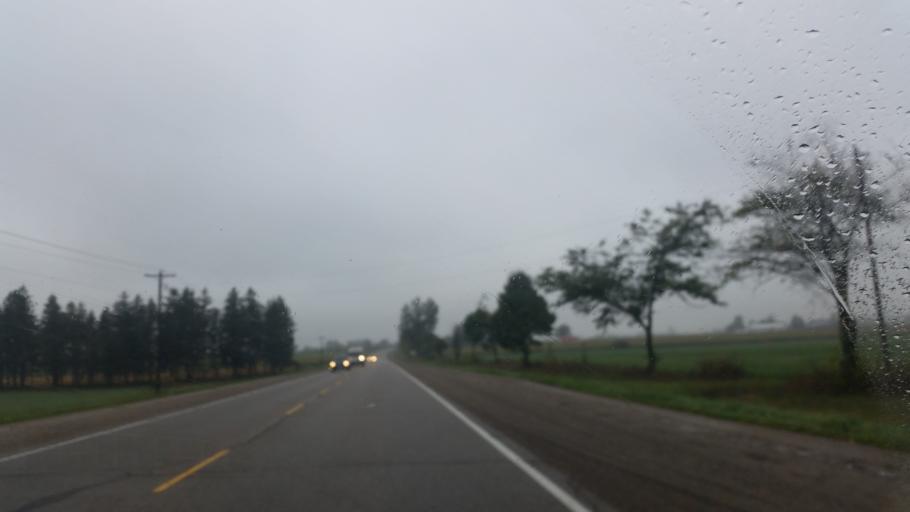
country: CA
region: Ontario
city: Waterloo
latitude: 43.5958
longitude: -80.5171
